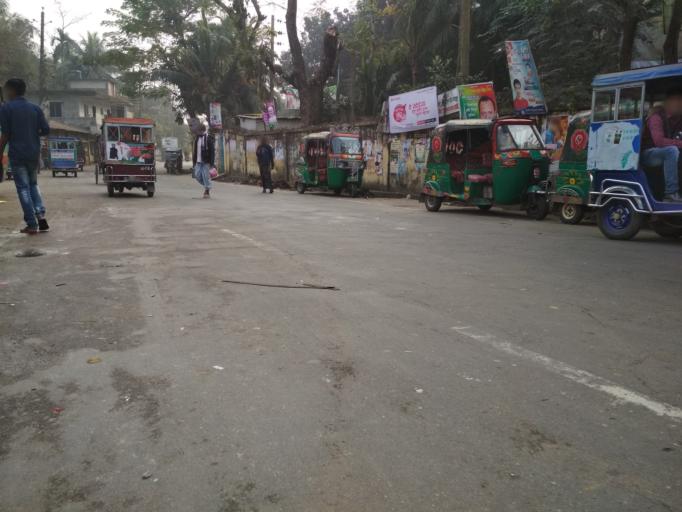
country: BD
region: Chittagong
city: Lakshmipur
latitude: 22.9419
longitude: 90.8417
